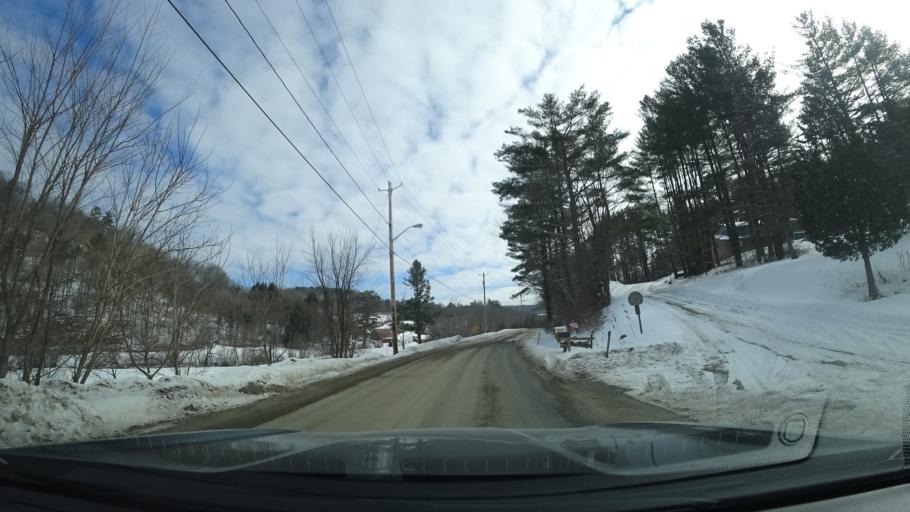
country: US
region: New York
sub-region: Washington County
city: Greenwich
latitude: 43.2281
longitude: -73.3701
